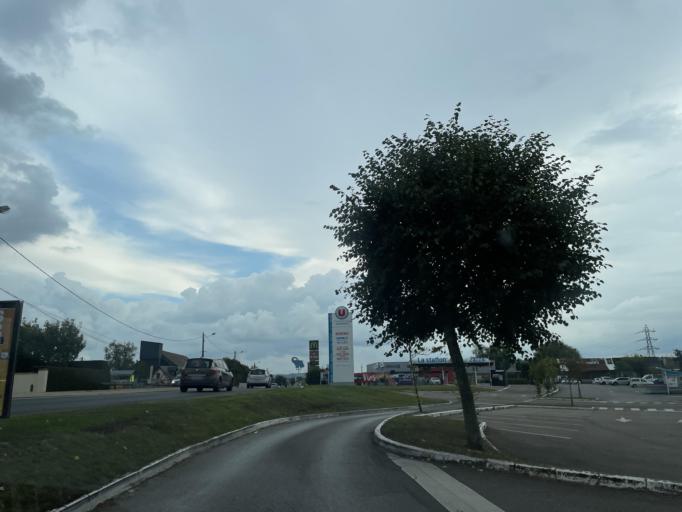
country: FR
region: Haute-Normandie
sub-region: Departement de la Seine-Maritime
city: Gournay-en-Bray
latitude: 49.4792
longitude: 1.7396
